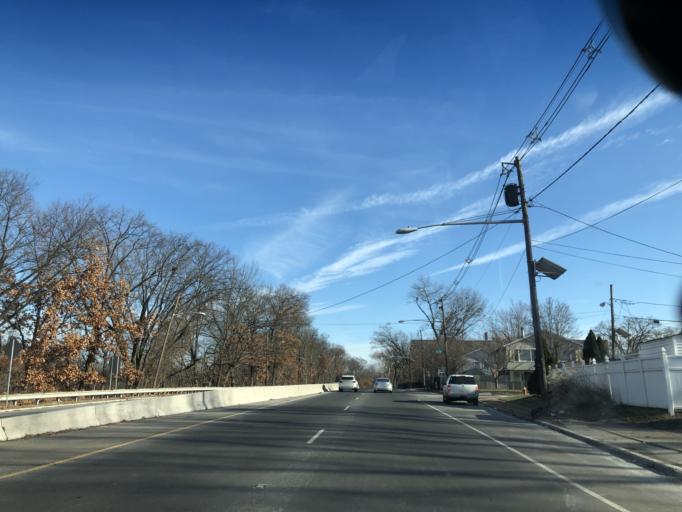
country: US
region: New Jersey
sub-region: Bergen County
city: Fair Lawn
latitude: 40.9223
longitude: -74.1389
